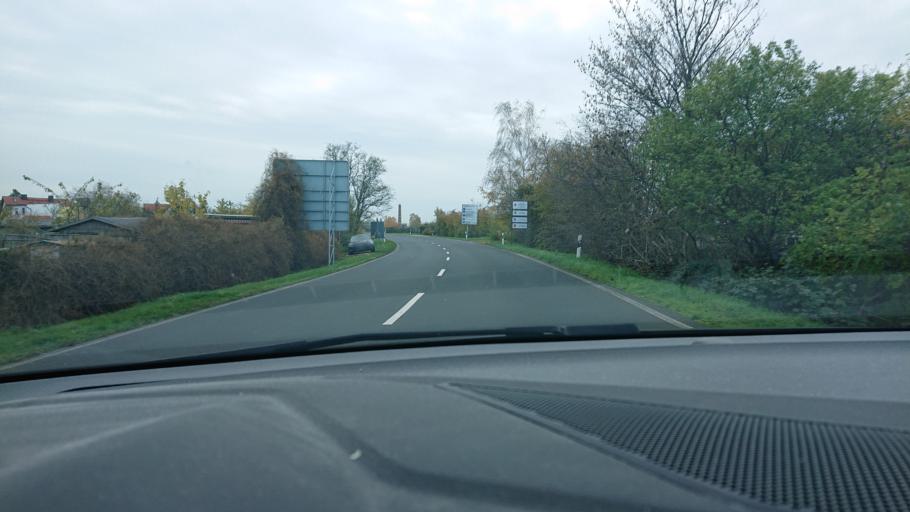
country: DE
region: Saxony
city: Delitzsch
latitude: 51.5235
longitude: 12.3129
